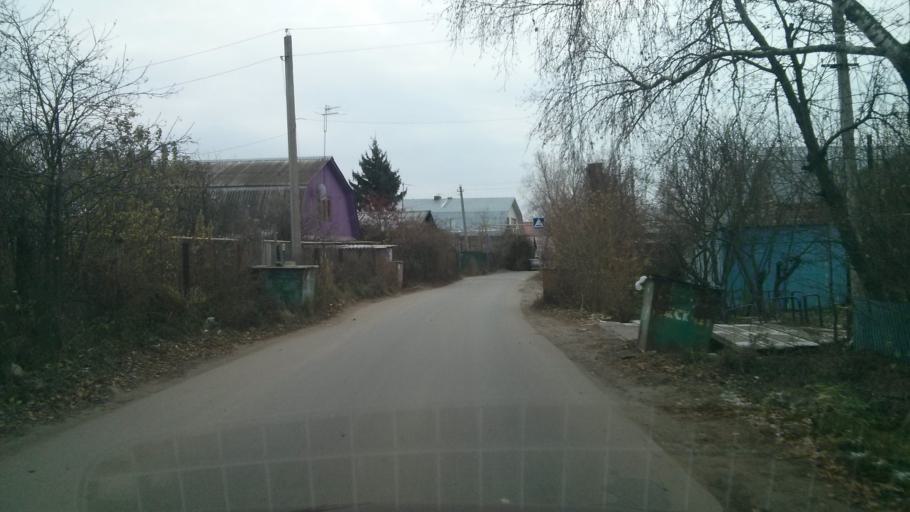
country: RU
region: Nizjnij Novgorod
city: Afonino
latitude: 56.2911
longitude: 44.1001
